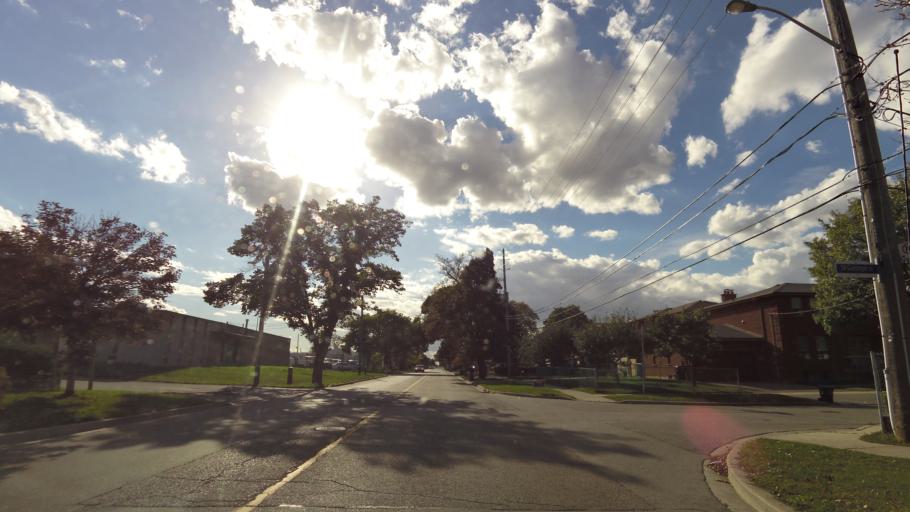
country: CA
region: Ontario
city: Etobicoke
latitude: 43.6149
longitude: -79.5028
